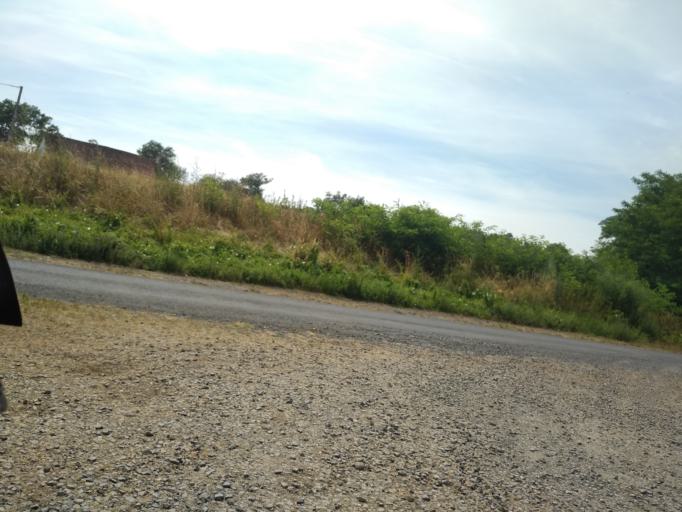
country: FR
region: Auvergne
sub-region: Departement de l'Allier
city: Diou
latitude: 46.5265
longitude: 3.7747
